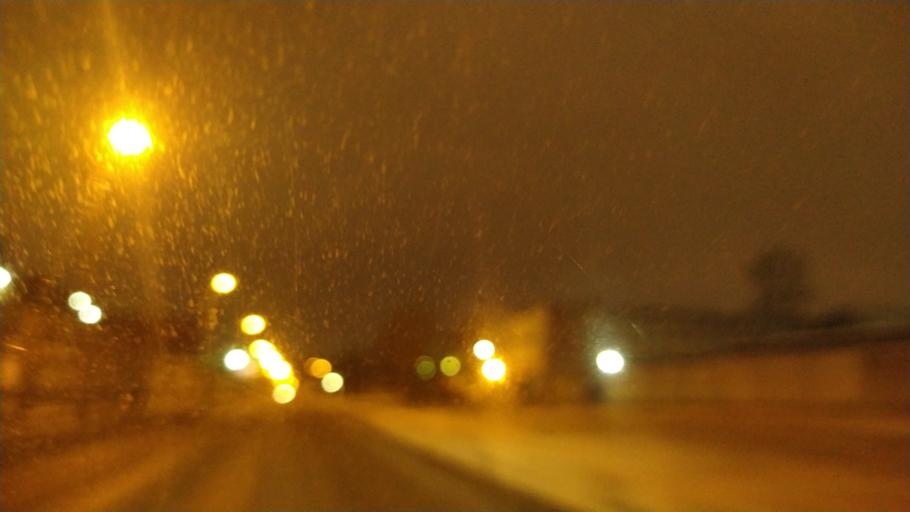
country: RU
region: St.-Petersburg
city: Kupchino
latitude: 59.8819
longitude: 30.3349
